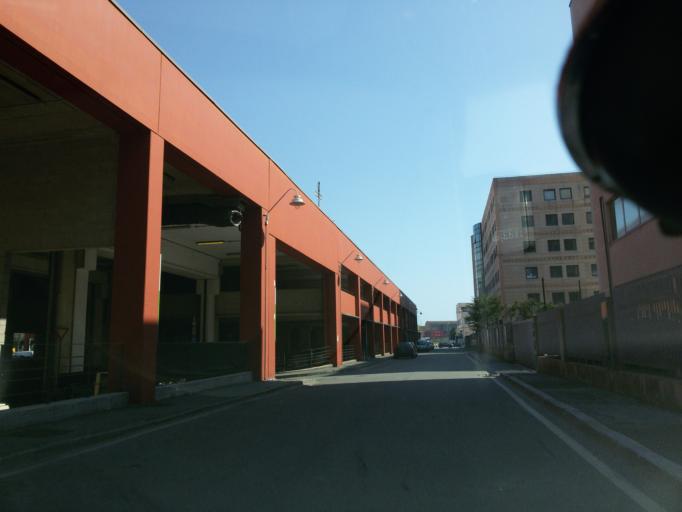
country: IT
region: Liguria
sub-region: Provincia di Genova
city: San Teodoro
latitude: 44.4219
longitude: 8.8799
